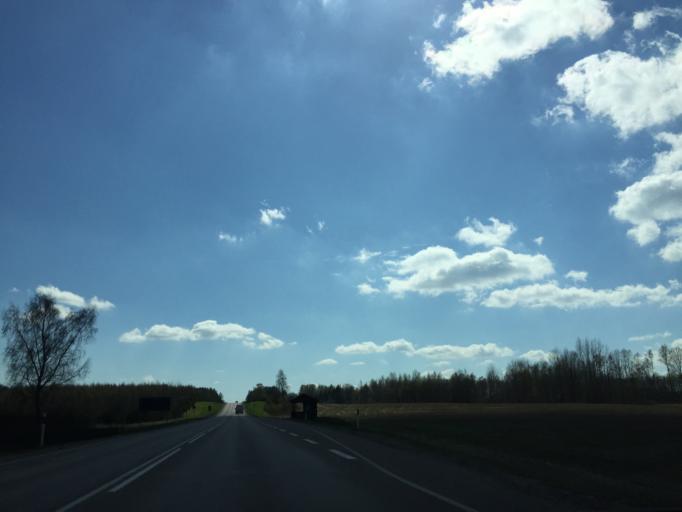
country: EE
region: Tartu
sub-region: Elva linn
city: Elva
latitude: 58.0818
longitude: 26.2087
